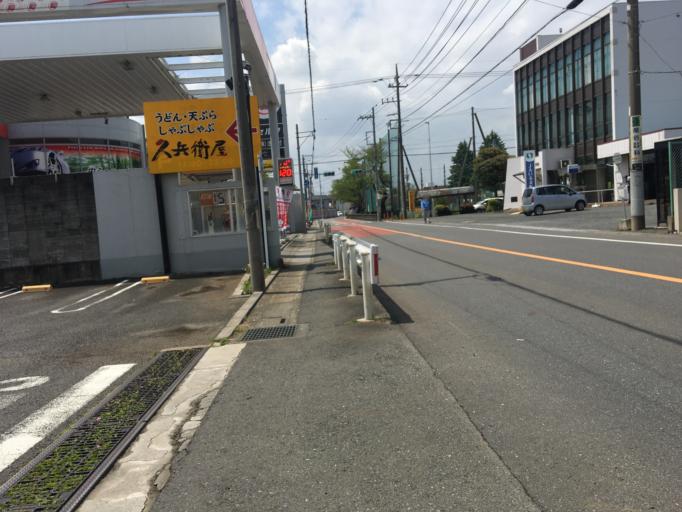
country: JP
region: Saitama
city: Shiki
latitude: 35.8416
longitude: 139.5615
